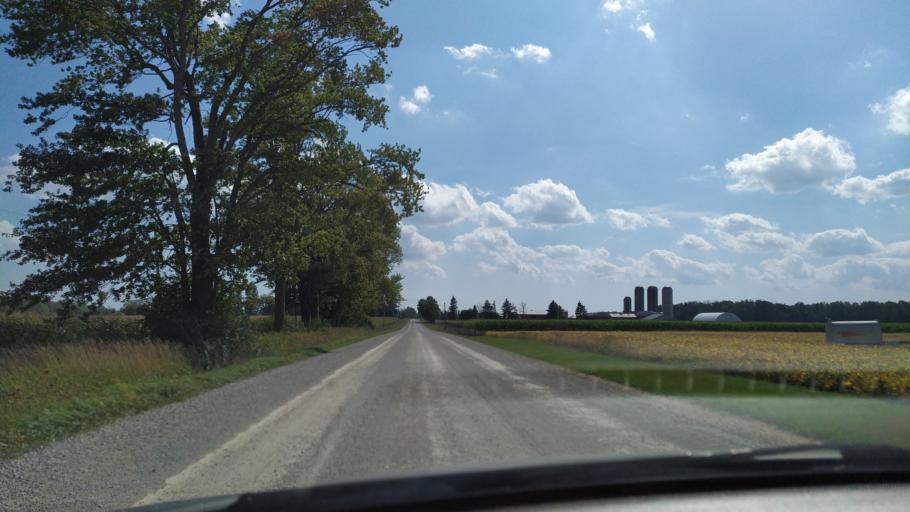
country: CA
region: Ontario
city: Stratford
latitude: 43.2753
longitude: -80.9239
